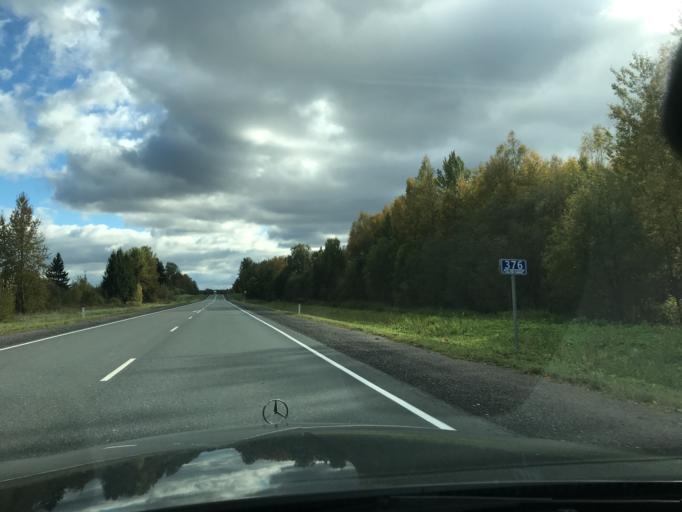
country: RU
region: Pskov
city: Pushkinskiye Gory
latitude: 57.0294
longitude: 28.5993
